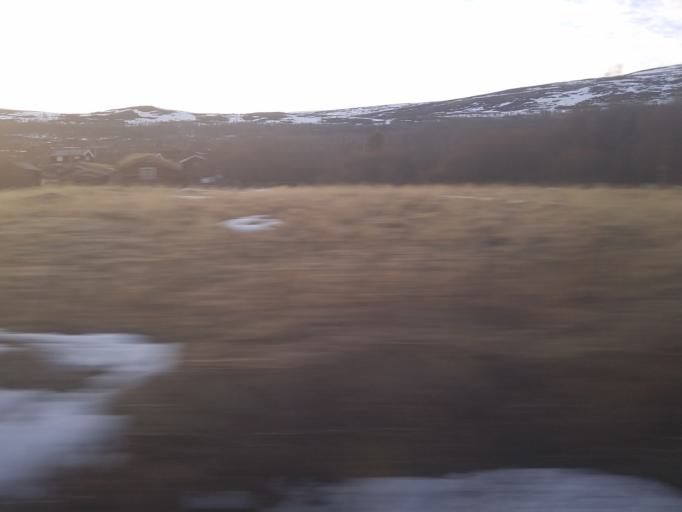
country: NO
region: Oppland
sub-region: Dovre
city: Dovre
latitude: 62.1744
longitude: 9.3813
